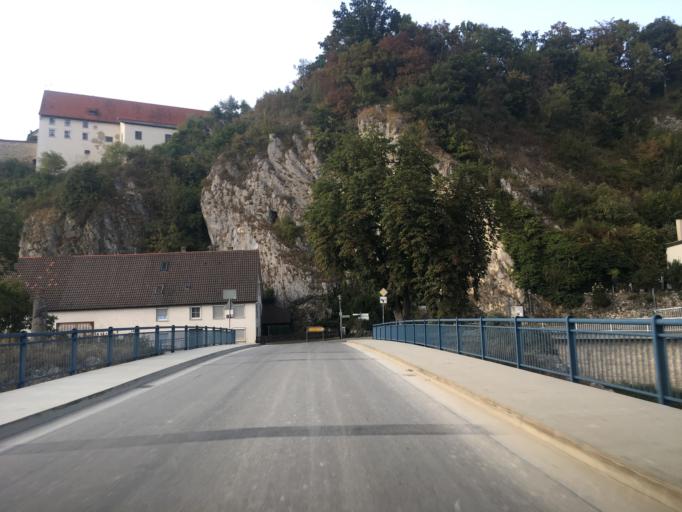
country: DE
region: Baden-Wuerttemberg
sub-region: Tuebingen Region
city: Rechtenstein
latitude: 48.2401
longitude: 9.5472
